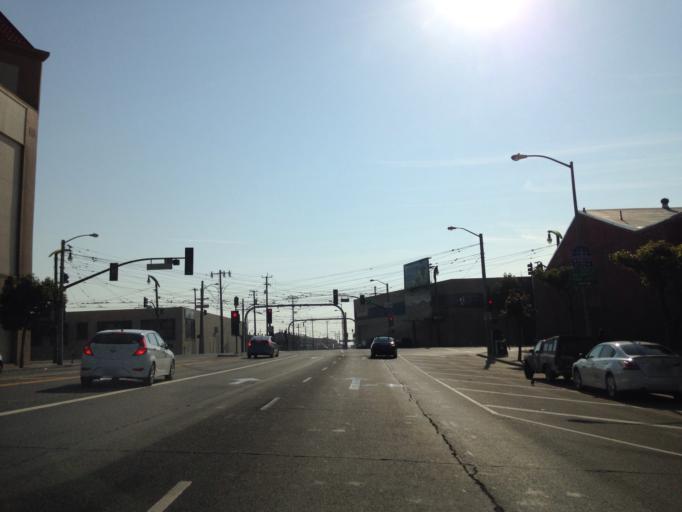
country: US
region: California
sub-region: San Francisco County
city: San Francisco
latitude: 37.7501
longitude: -122.3883
